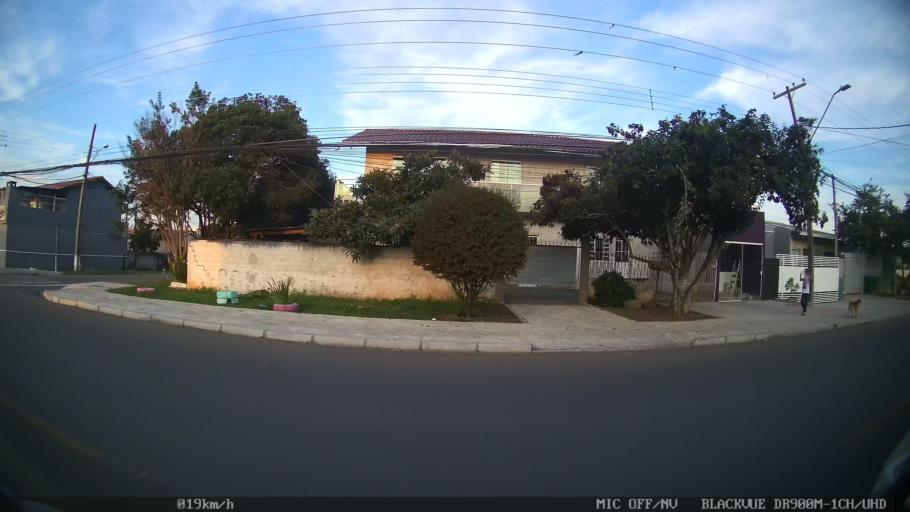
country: BR
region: Parana
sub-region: Pinhais
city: Pinhais
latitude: -25.4629
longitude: -49.1864
